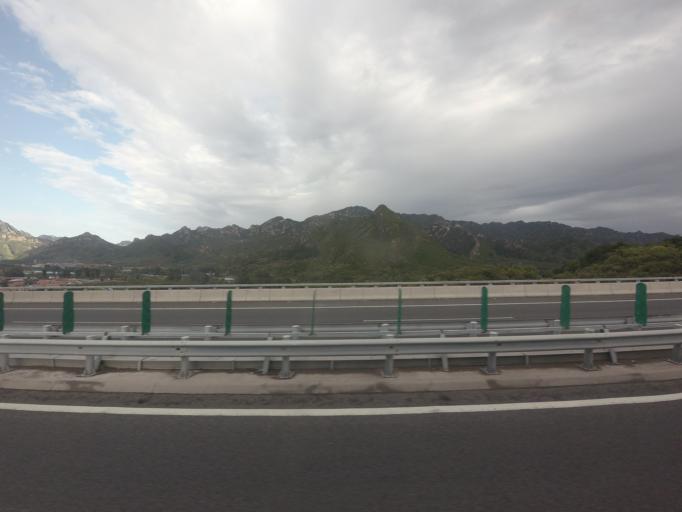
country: CN
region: Beijing
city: Beizhuang
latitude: 40.4767
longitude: 117.1628
